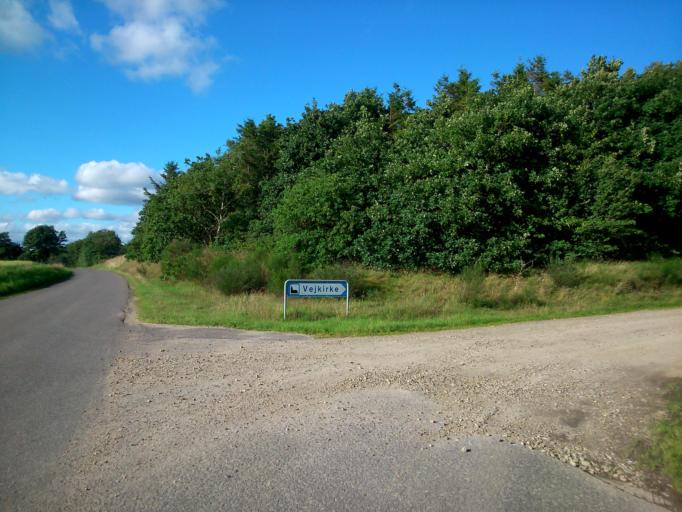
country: DK
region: Central Jutland
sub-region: Herning Kommune
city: Snejbjerg
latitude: 56.1869
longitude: 8.8453
